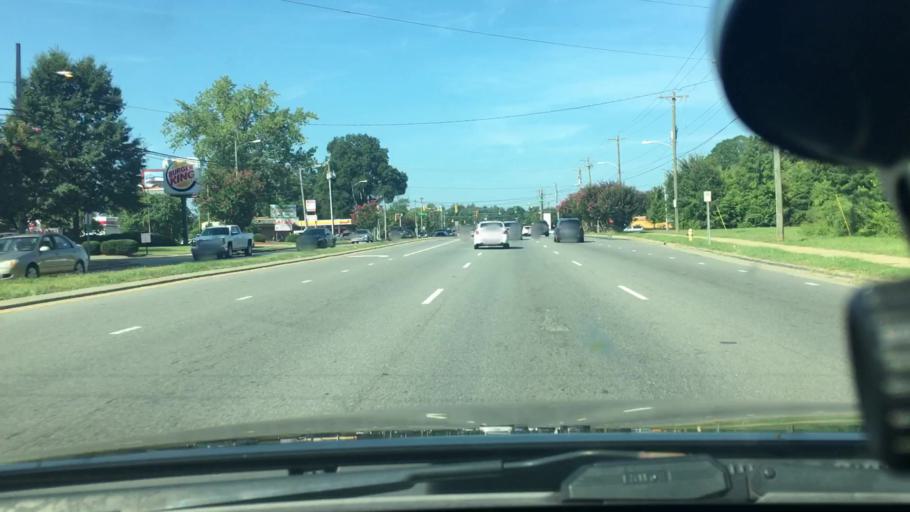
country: US
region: North Carolina
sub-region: Mecklenburg County
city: Mint Hill
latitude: 35.2038
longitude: -80.7222
